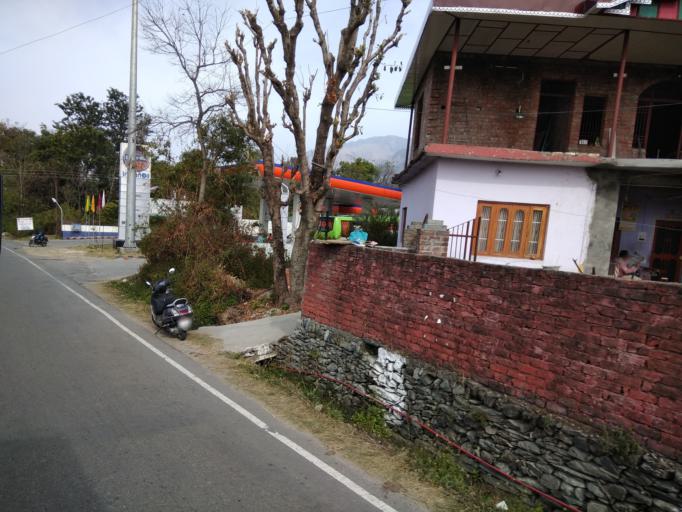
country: IN
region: Himachal Pradesh
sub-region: Kangra
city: Dharmsala
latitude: 32.1648
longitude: 76.3969
